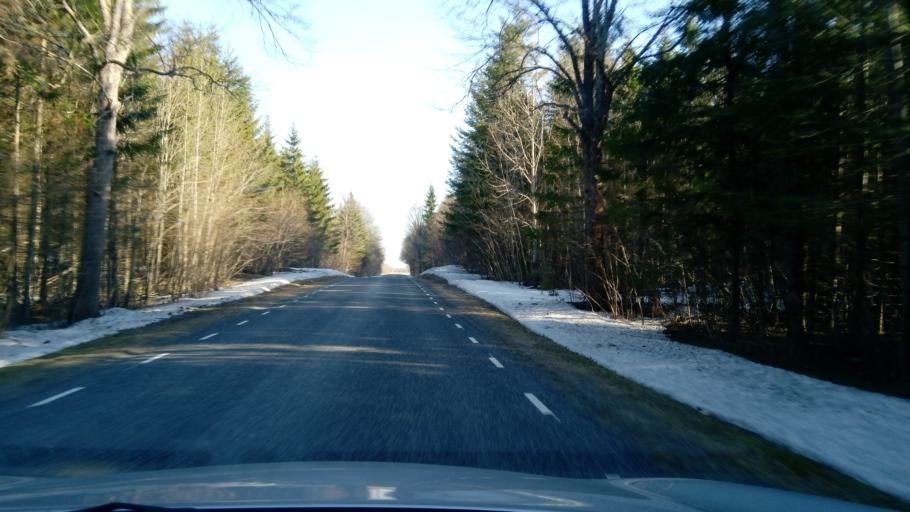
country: EE
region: Laeaene-Virumaa
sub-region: Tamsalu vald
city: Tamsalu
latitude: 59.1975
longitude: 26.1329
